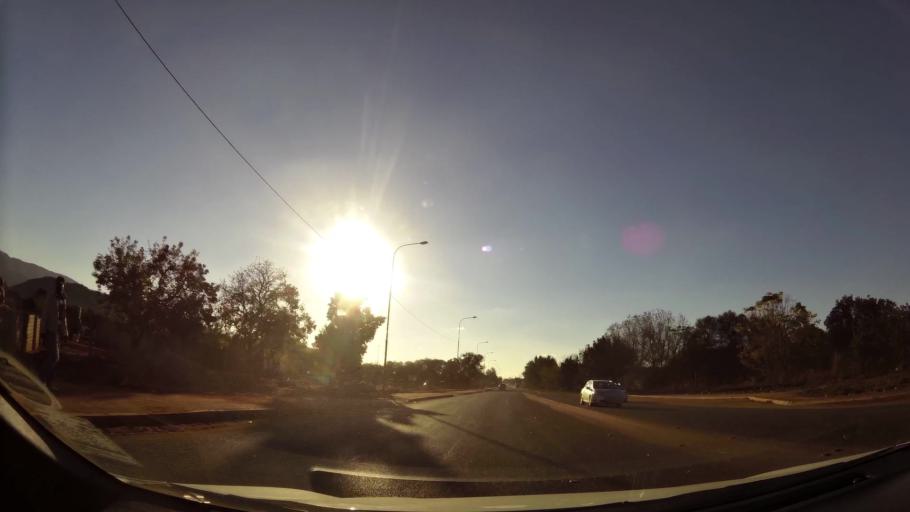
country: ZA
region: Limpopo
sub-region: Waterberg District Municipality
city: Mokopane
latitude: -24.1583
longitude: 28.9874
